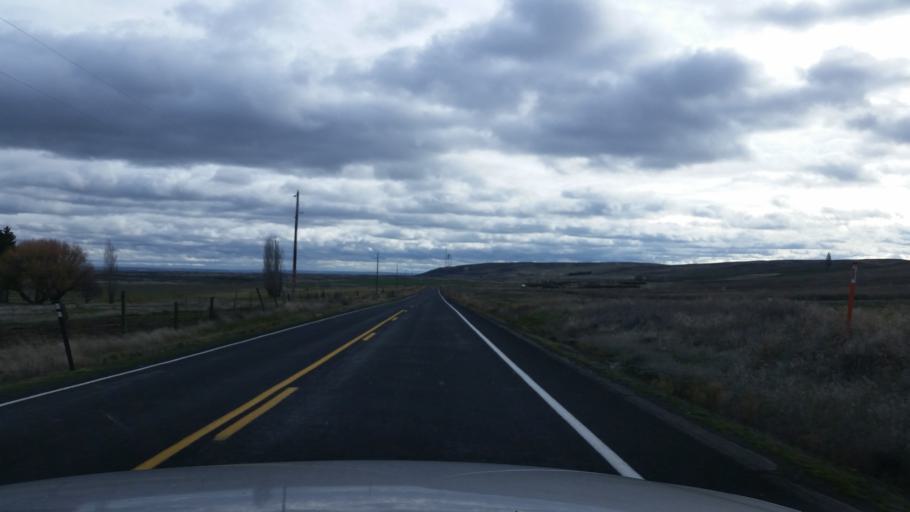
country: US
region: Washington
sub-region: Lincoln County
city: Davenport
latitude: 47.3401
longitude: -118.0041
